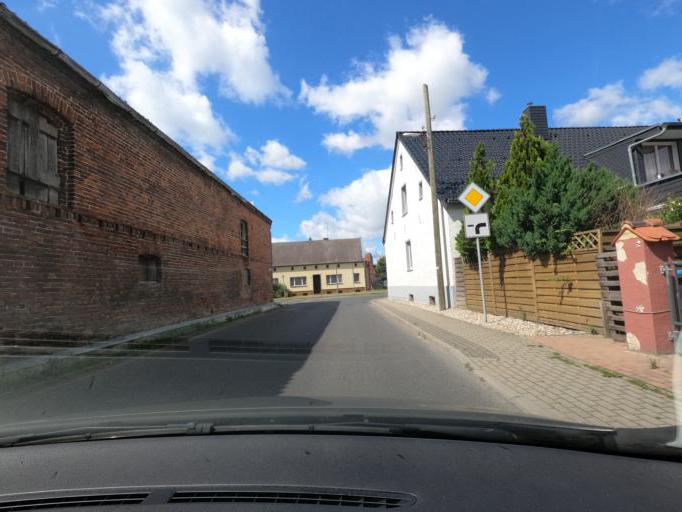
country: DE
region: Brandenburg
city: Kremmen
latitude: 52.7283
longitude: 12.9556
